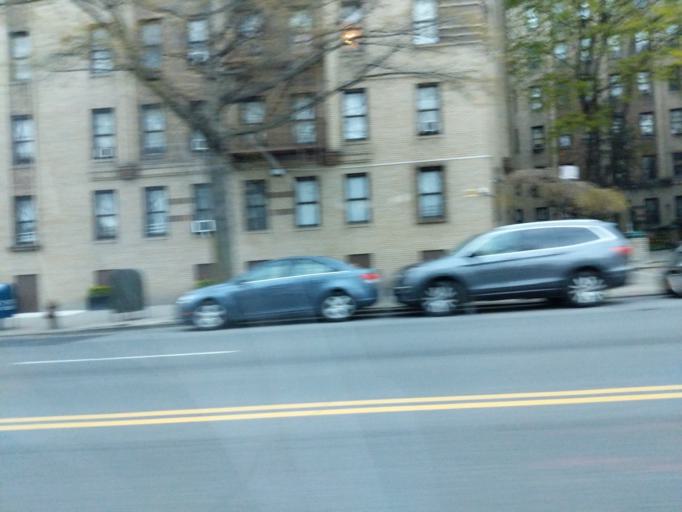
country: US
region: New York
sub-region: Bronx
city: The Bronx
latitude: 40.8535
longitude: -73.8691
